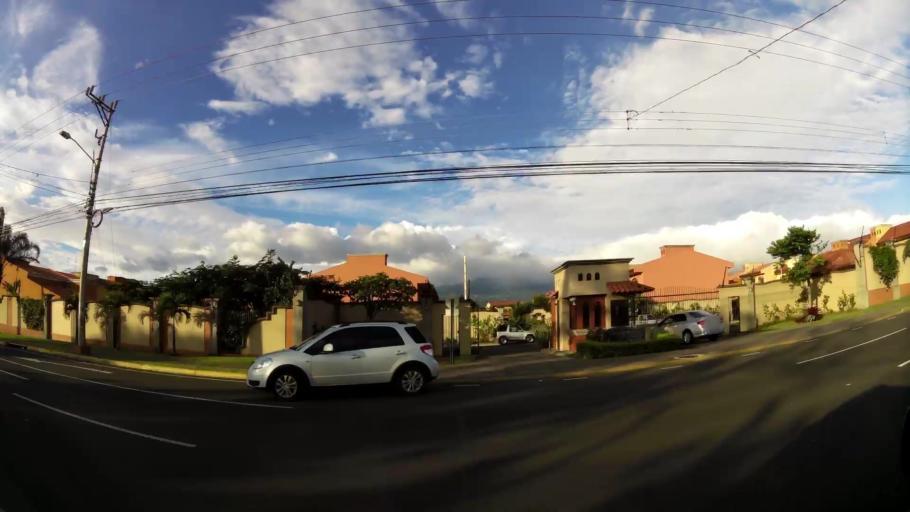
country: CR
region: Heredia
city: Llorente
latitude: 10.0020
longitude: -84.1577
